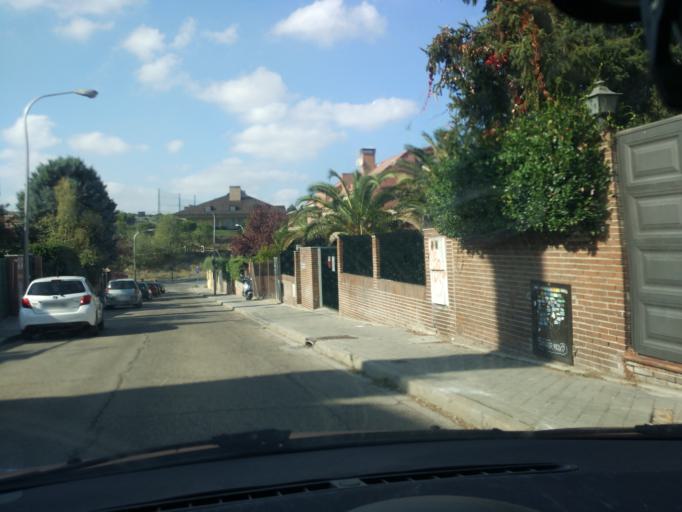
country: ES
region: Madrid
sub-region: Provincia de Madrid
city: Fuencarral-El Pardo
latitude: 40.4840
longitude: -3.7349
